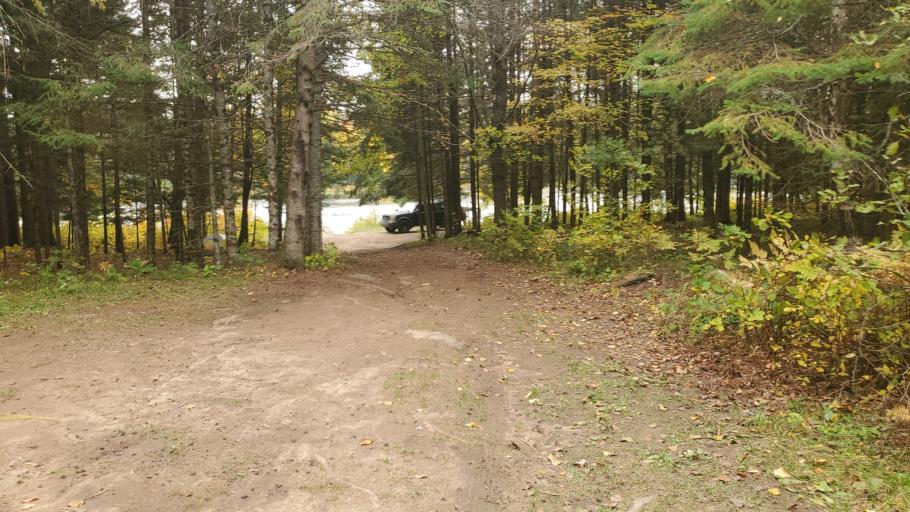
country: CA
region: Ontario
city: Renfrew
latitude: 45.2600
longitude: -77.2003
